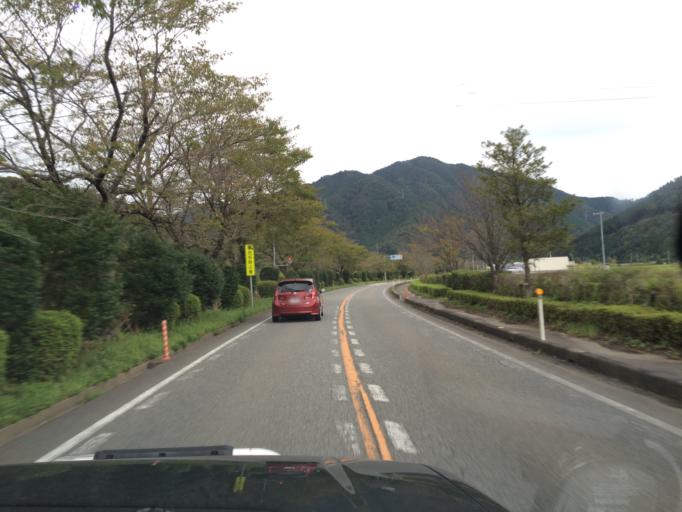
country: JP
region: Hyogo
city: Toyooka
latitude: 35.3765
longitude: 134.8134
